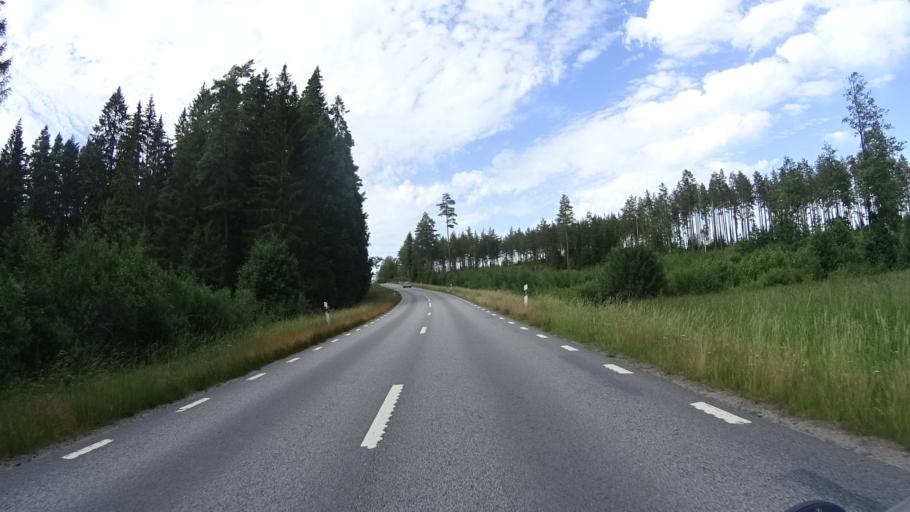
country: SE
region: OEstergoetland
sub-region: Atvidabergs Kommun
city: Atvidaberg
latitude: 58.1319
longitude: 16.0926
